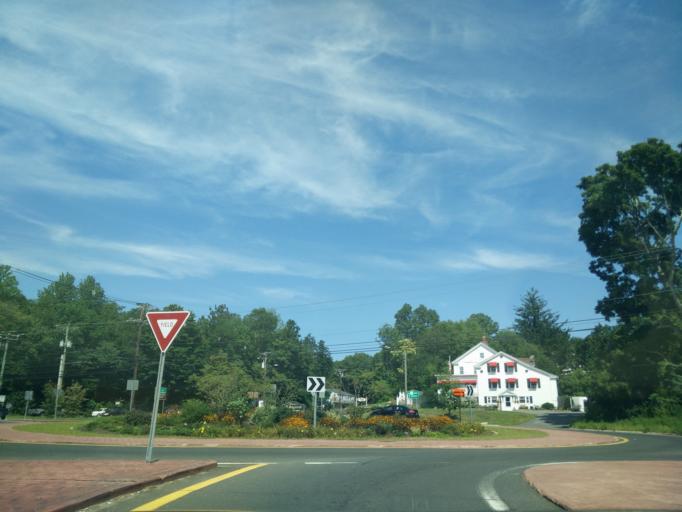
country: US
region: Connecticut
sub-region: New Haven County
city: Madison
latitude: 41.3578
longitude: -72.5649
